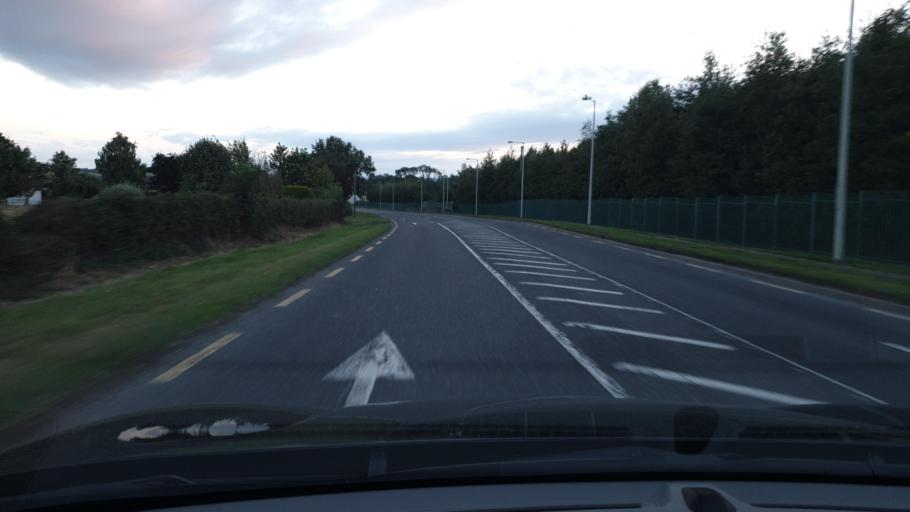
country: IE
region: Leinster
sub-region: An Mhi
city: Duleek
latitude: 53.6763
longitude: -6.3899
